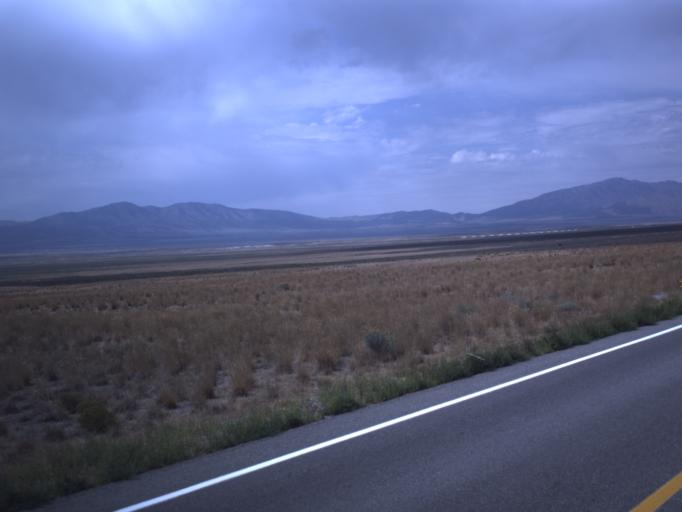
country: US
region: Utah
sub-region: Utah County
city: Eagle Mountain
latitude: 40.2704
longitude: -112.2441
